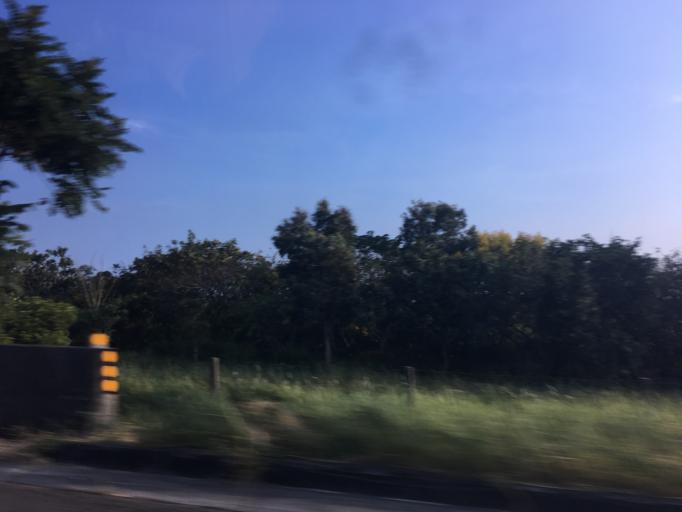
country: TW
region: Taiwan
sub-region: Chiayi
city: Taibao
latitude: 23.4279
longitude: 120.3379
